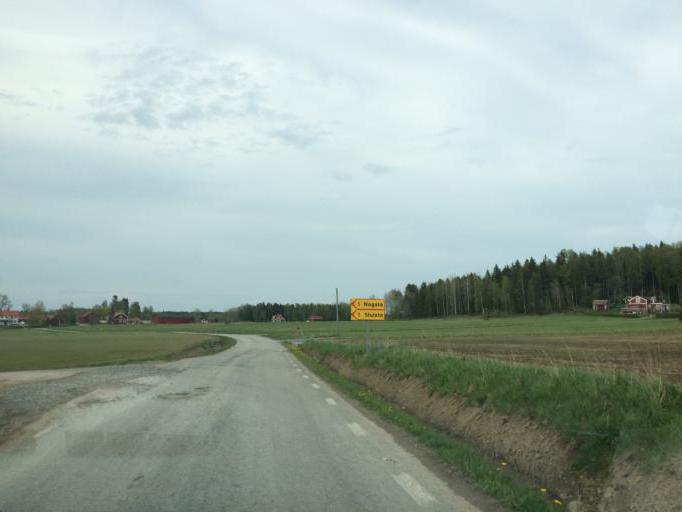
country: SE
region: Vaestmanland
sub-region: Kopings Kommun
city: Koping
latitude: 59.6094
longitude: 16.0273
